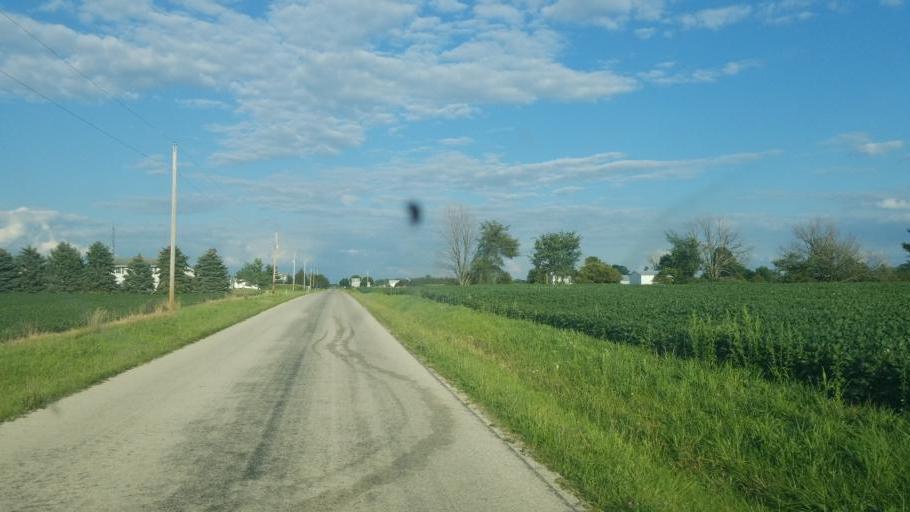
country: US
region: Ohio
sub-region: Seneca County
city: Tiffin
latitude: 41.1096
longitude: -83.0700
